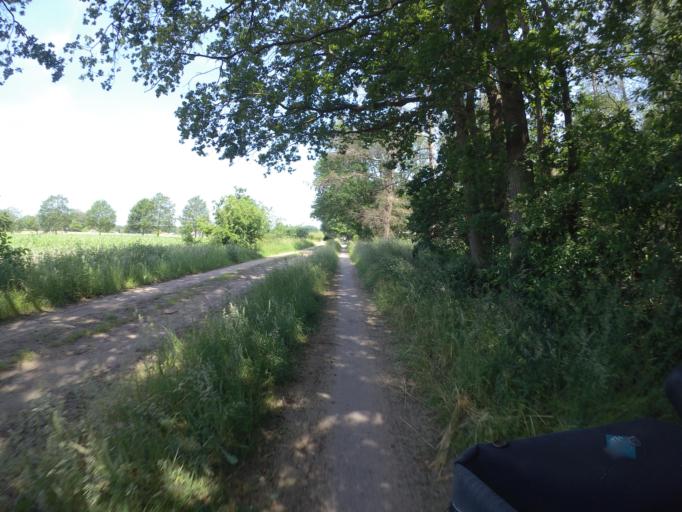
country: NL
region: Overijssel
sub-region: Gemeente Hof van Twente
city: Markelo
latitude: 52.2309
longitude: 6.5239
